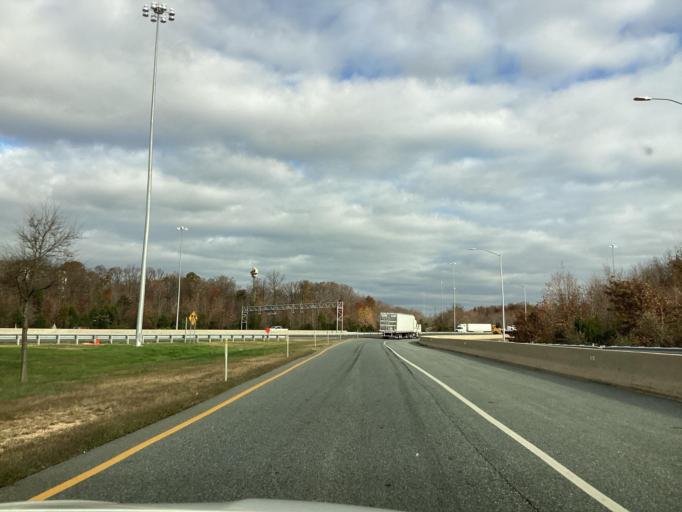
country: US
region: Maryland
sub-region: Cecil County
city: Perryville
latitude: 39.5889
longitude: -76.0704
